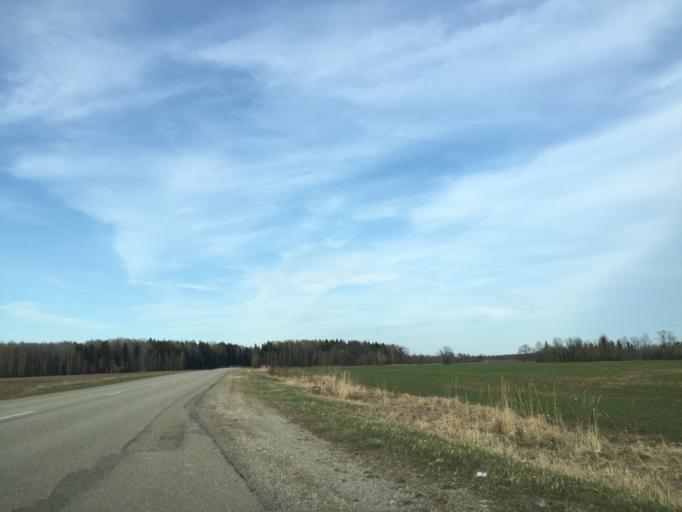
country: LV
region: Lielvarde
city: Lielvarde
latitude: 56.7876
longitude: 24.8014
